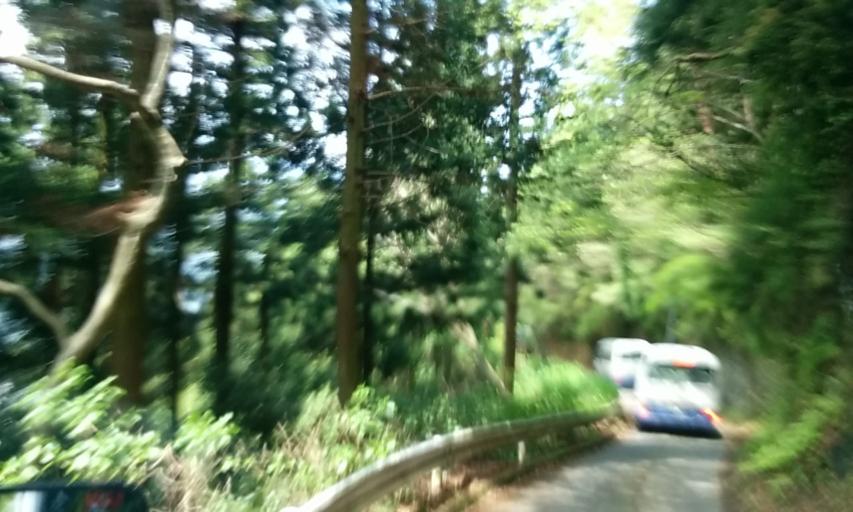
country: JP
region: Ehime
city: Niihama
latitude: 33.8786
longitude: 133.3109
